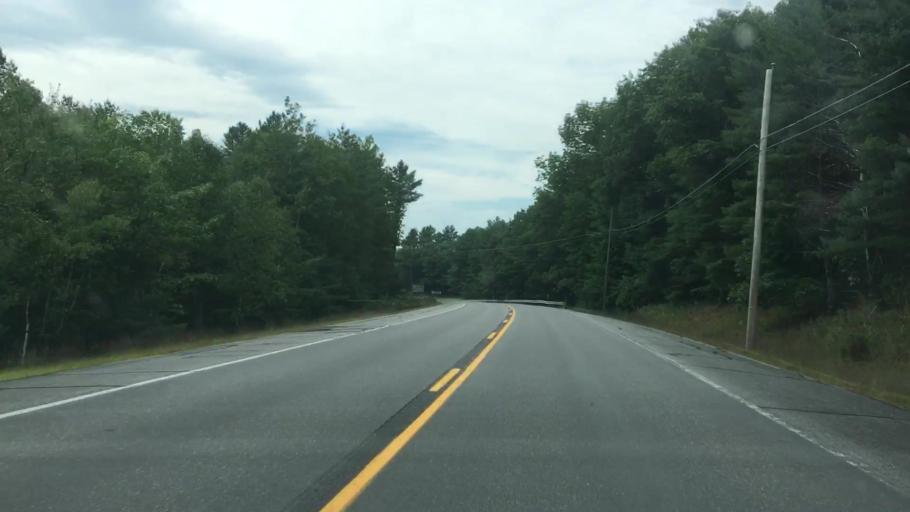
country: US
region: Maine
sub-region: Oxford County
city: Bethel
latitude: 44.4876
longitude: -70.7689
